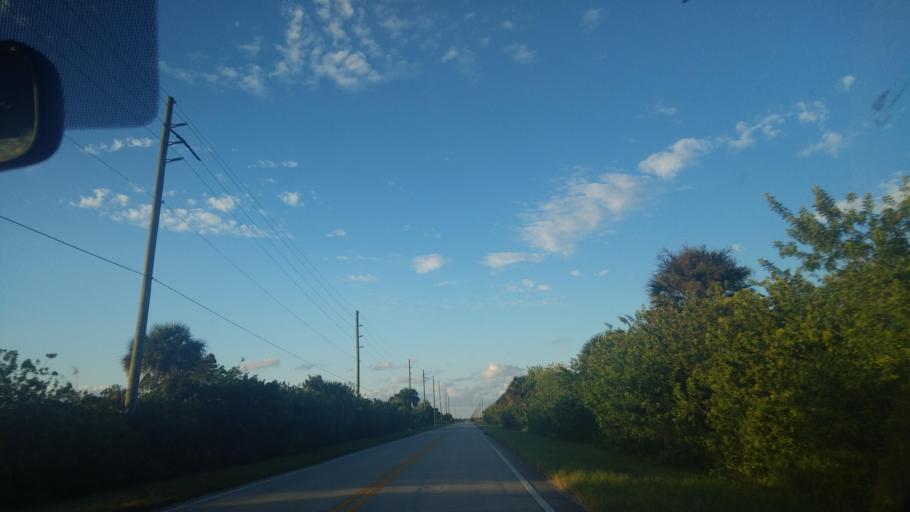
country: US
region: Florida
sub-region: Indian River County
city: Fellsmere
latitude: 27.6964
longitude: -80.6429
